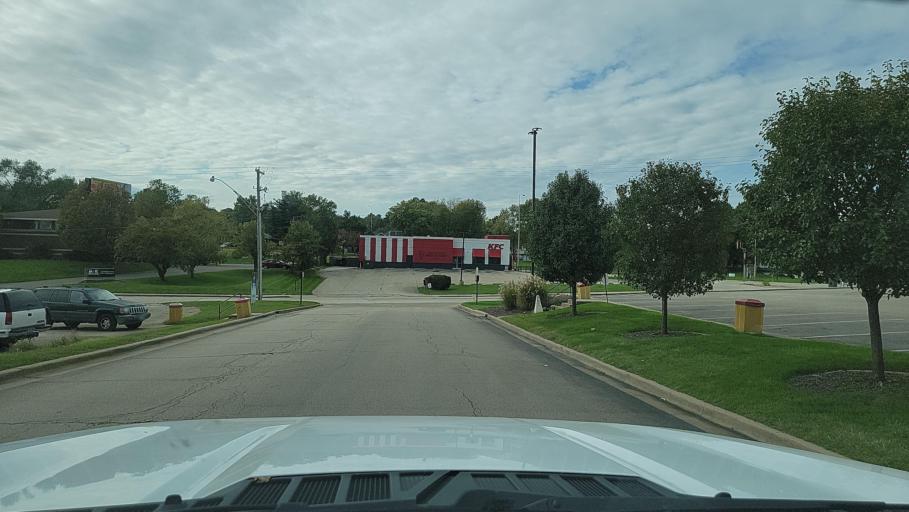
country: US
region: Illinois
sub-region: Peoria County
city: Bartonville
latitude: 40.6528
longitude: -89.6475
